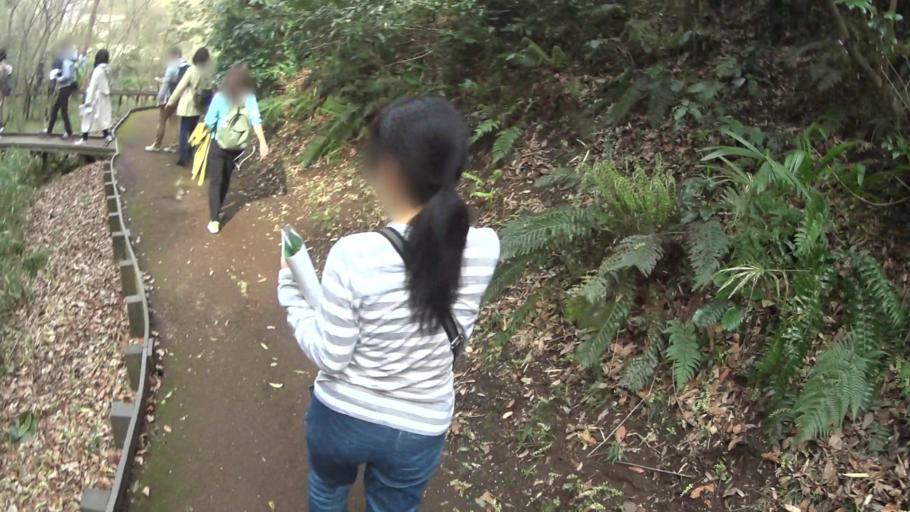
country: JP
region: Kanagawa
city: Kamakura
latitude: 35.3189
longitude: 139.5163
